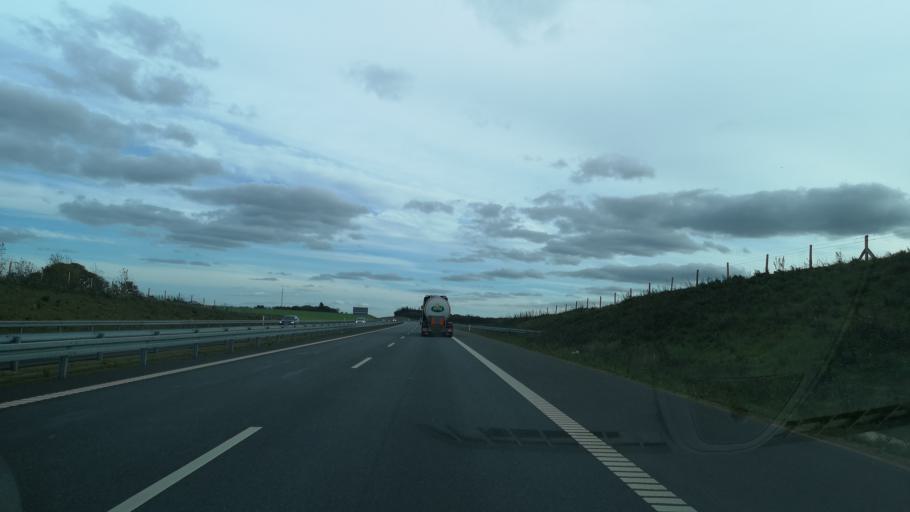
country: DK
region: Central Jutland
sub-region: Herning Kommune
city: Avlum
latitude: 56.2779
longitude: 8.7419
